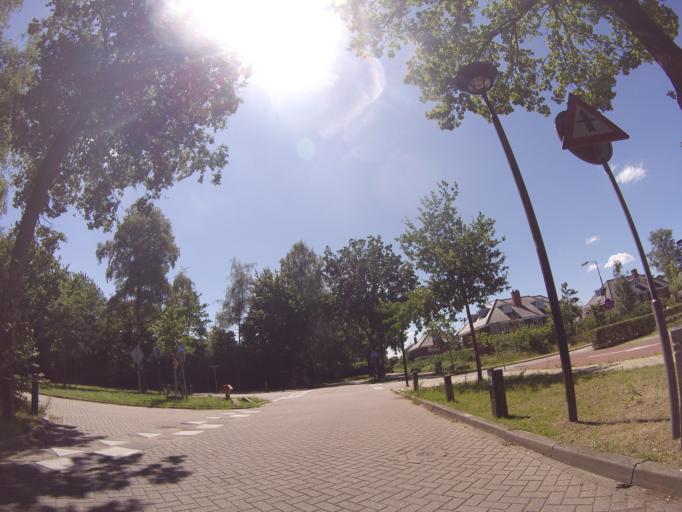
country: NL
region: Utrecht
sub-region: Gemeente De Bilt
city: De Bilt
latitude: 52.1339
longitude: 5.1957
